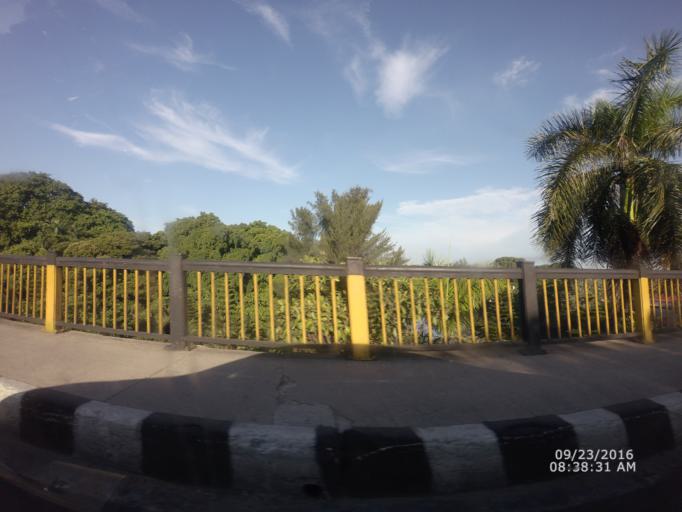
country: CU
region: La Habana
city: Havana
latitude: 23.1185
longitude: -82.4085
